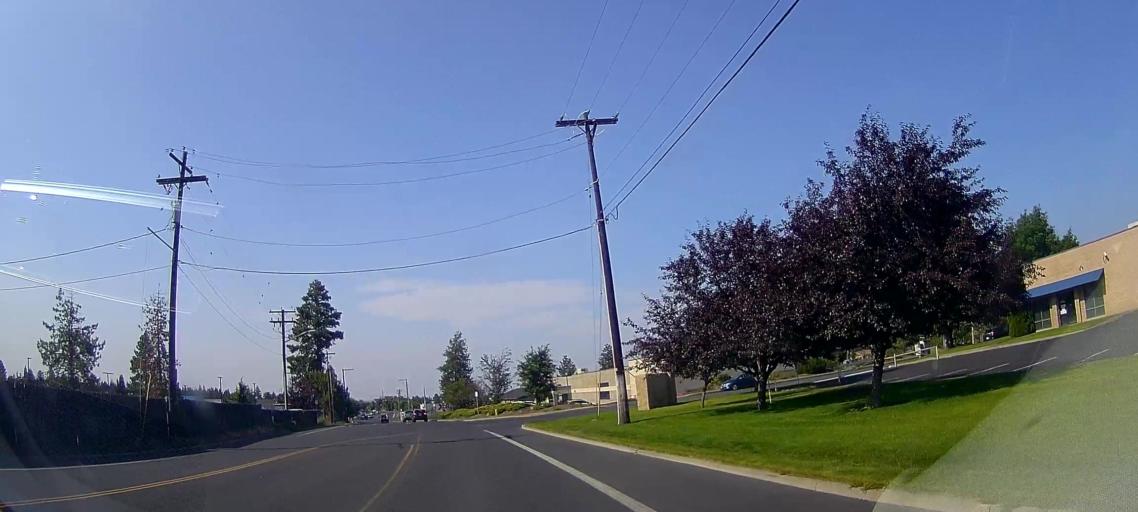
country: US
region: Oregon
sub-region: Deschutes County
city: Bend
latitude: 44.0527
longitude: -121.2686
